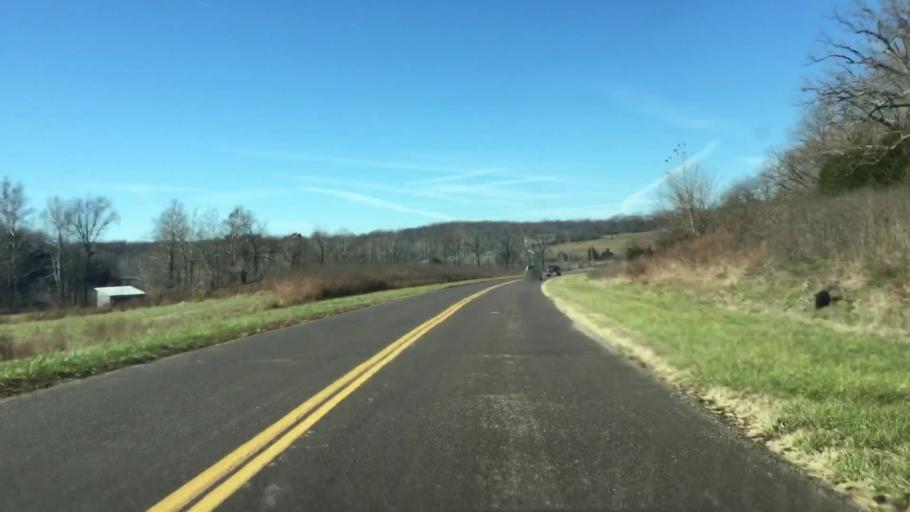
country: US
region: Missouri
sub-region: Miller County
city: Eldon
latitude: 38.3389
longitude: -92.7154
